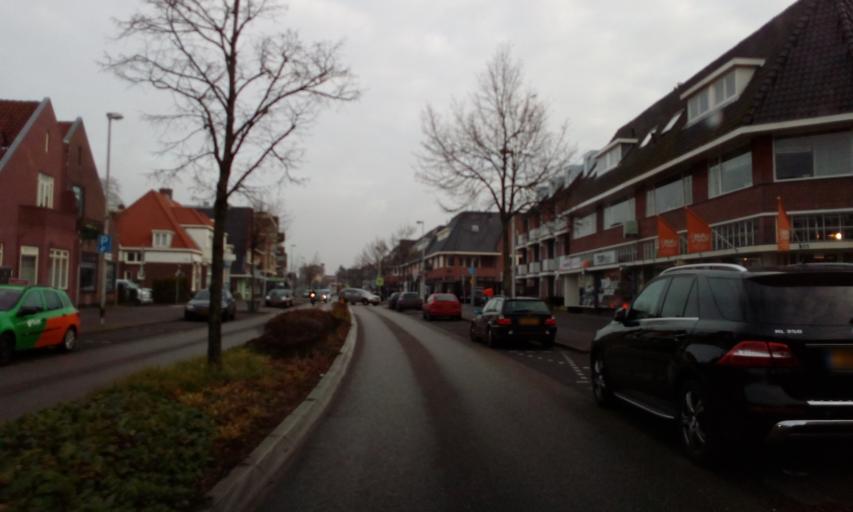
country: NL
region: North Holland
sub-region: Gemeente Bussum
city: Bussum
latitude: 52.2740
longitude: 5.1682
